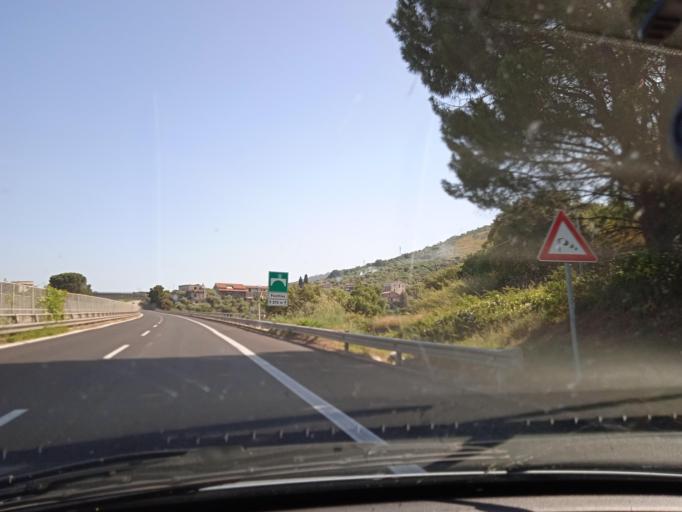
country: IT
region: Sicily
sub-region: Messina
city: Rocca di Capri Leone
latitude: 38.1156
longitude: 14.7257
